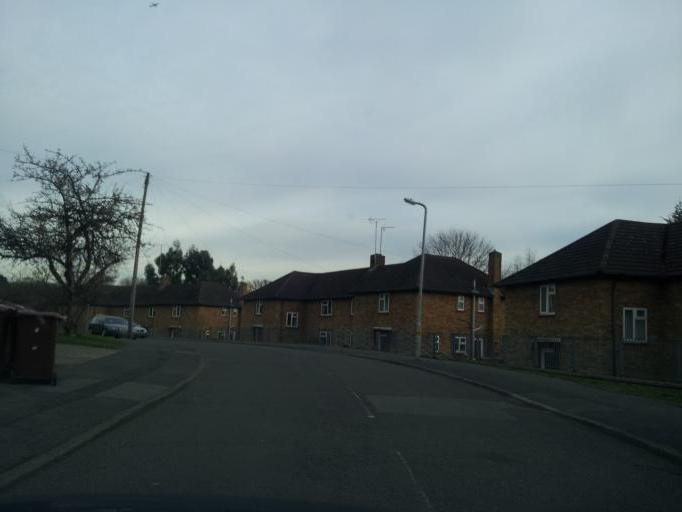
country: GB
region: England
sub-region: Hertfordshire
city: Bushey
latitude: 51.6338
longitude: -0.3503
